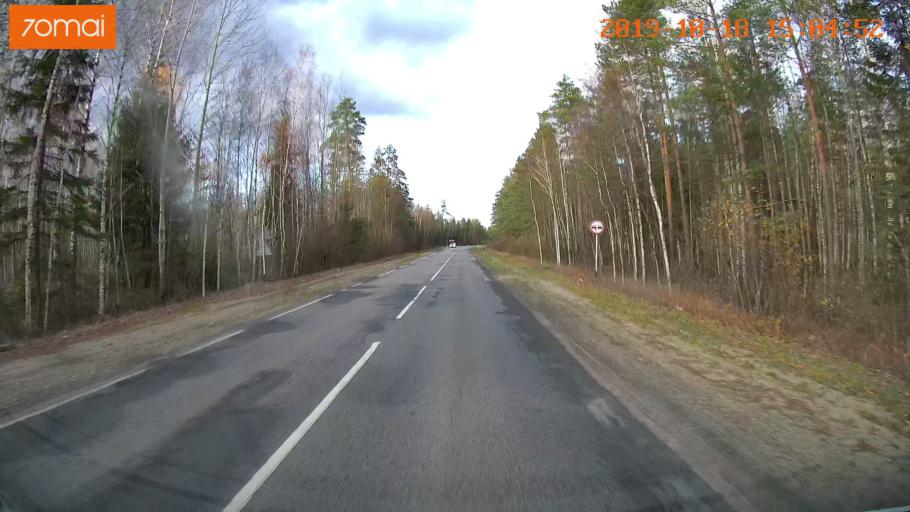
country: RU
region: Vladimir
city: Kurlovo
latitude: 55.5072
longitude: 40.5705
